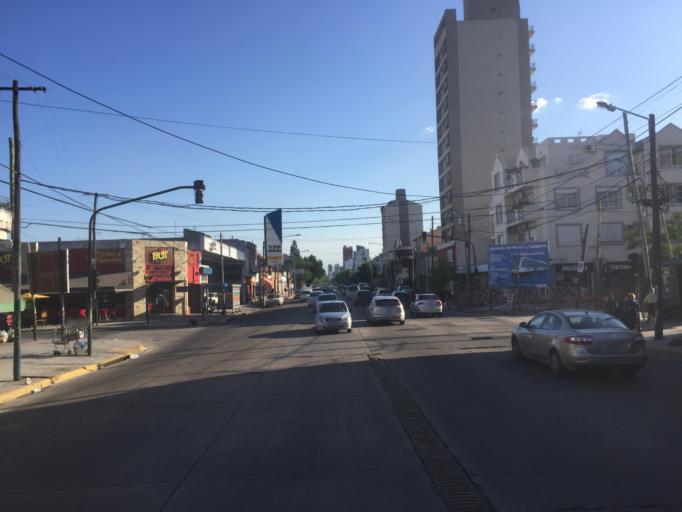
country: AR
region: Buenos Aires
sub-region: Partido de Lomas de Zamora
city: Lomas de Zamora
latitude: -34.7454
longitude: -58.3936
